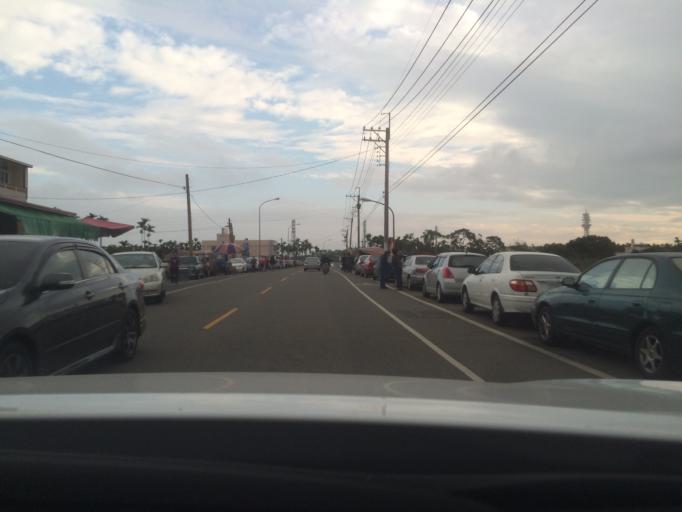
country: TW
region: Taiwan
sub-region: Nantou
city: Nantou
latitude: 23.9319
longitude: 120.6384
